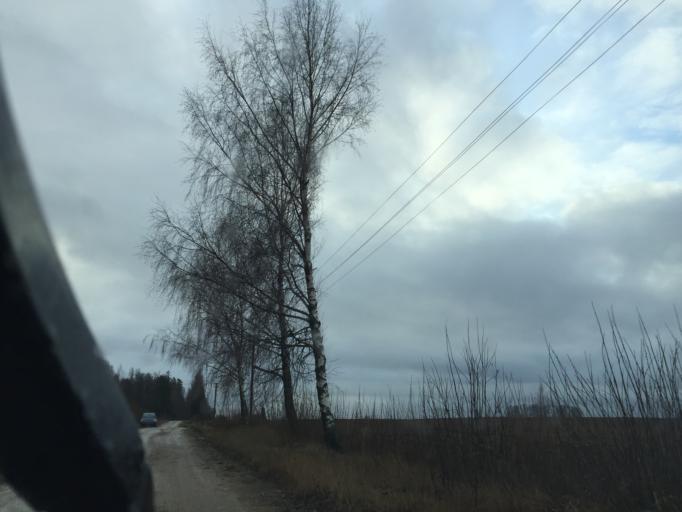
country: LV
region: Vainode
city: Vainode
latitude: 56.6087
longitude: 21.7982
